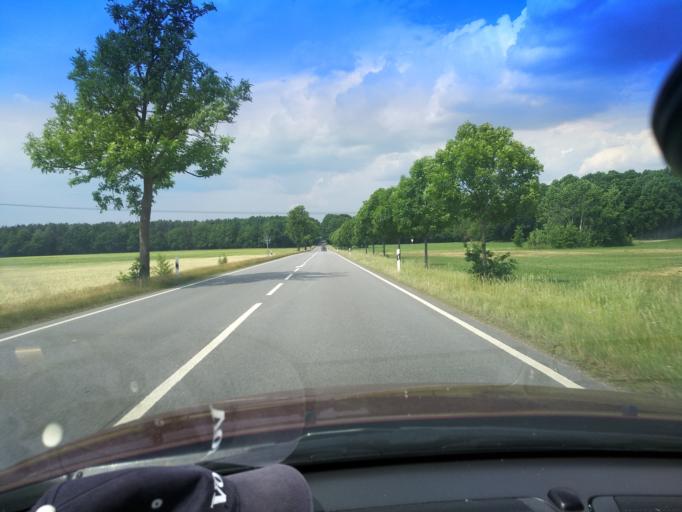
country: DE
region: Saxony
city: Niesky
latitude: 51.2738
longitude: 14.8339
